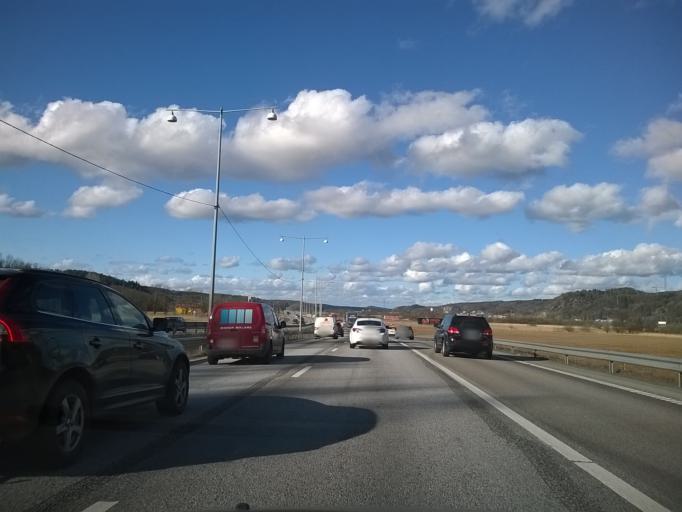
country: SE
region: Vaestra Goetaland
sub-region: Goteborg
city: Gardsten
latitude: 57.8018
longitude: 12.0079
